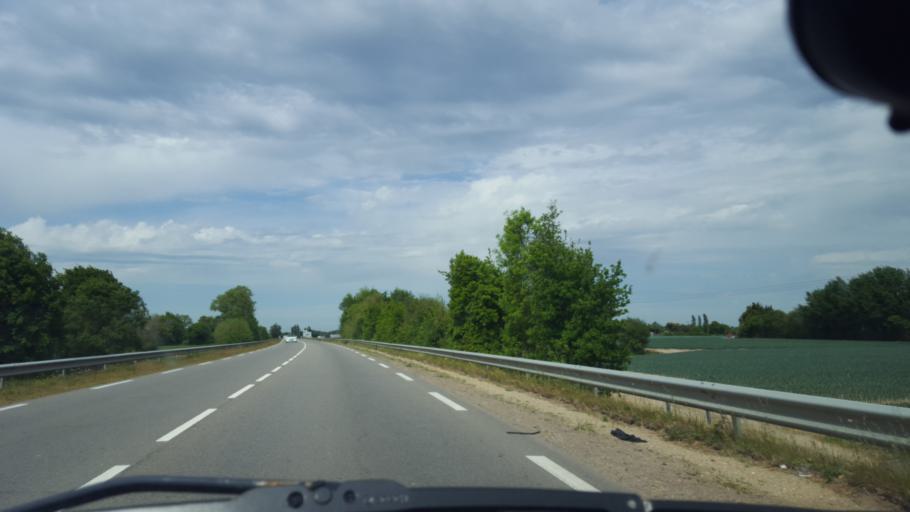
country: FR
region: Pays de la Loire
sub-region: Departement de la Loire-Atlantique
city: Machecoul
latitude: 46.9848
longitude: -1.7987
